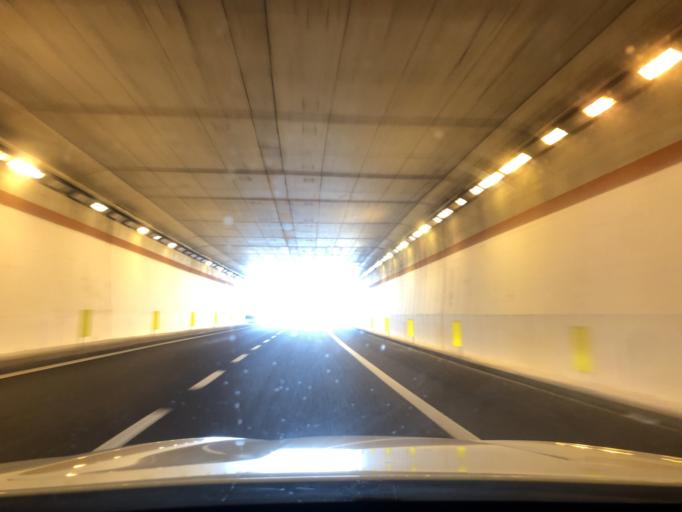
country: IT
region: Lombardy
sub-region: Citta metropolitana di Milano
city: Casate
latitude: 45.5025
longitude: 8.8335
